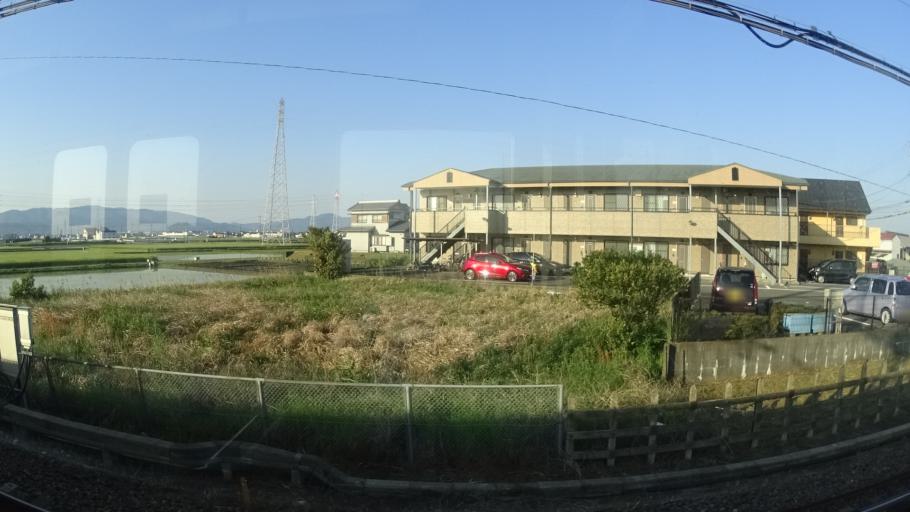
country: JP
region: Mie
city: Ise
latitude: 34.5206
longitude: 136.6710
